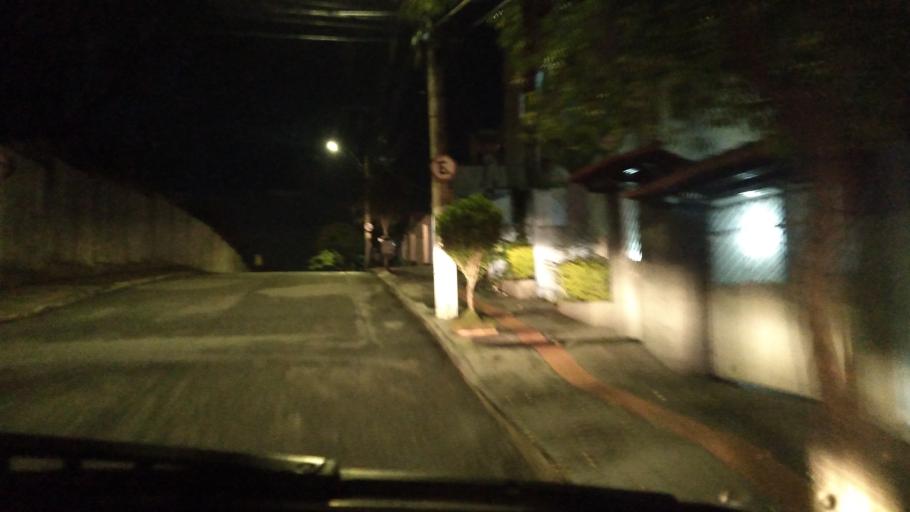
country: BR
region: Minas Gerais
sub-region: Belo Horizonte
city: Belo Horizonte
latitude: -19.8722
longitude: -43.9387
